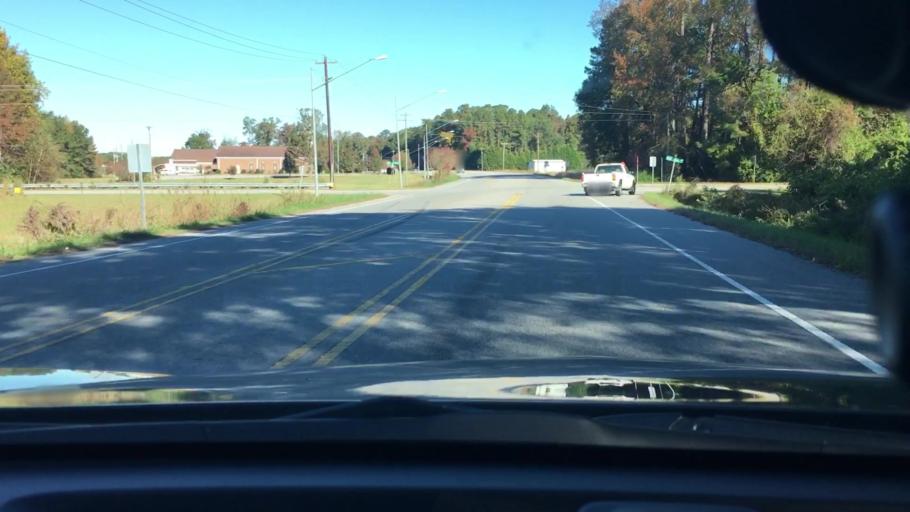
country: US
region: North Carolina
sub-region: Edgecombe County
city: Tarboro
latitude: 35.9167
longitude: -77.5624
